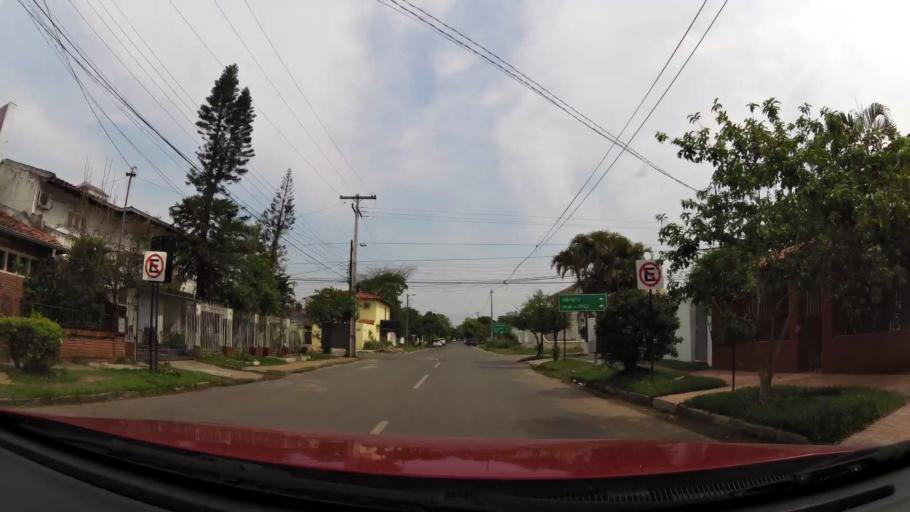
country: PY
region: Central
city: Fernando de la Mora
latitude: -25.2783
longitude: -57.5494
